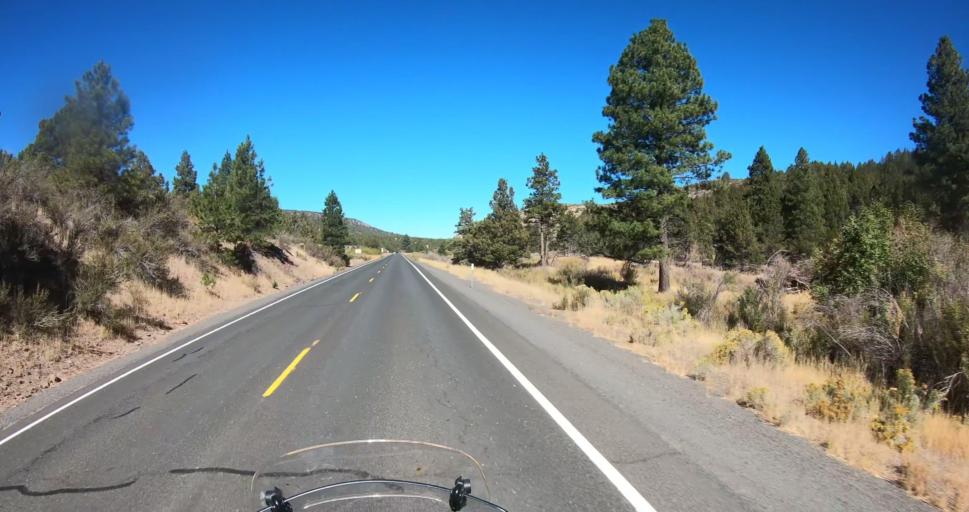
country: US
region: Oregon
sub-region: Lake County
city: Lakeview
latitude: 42.4156
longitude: -120.2899
